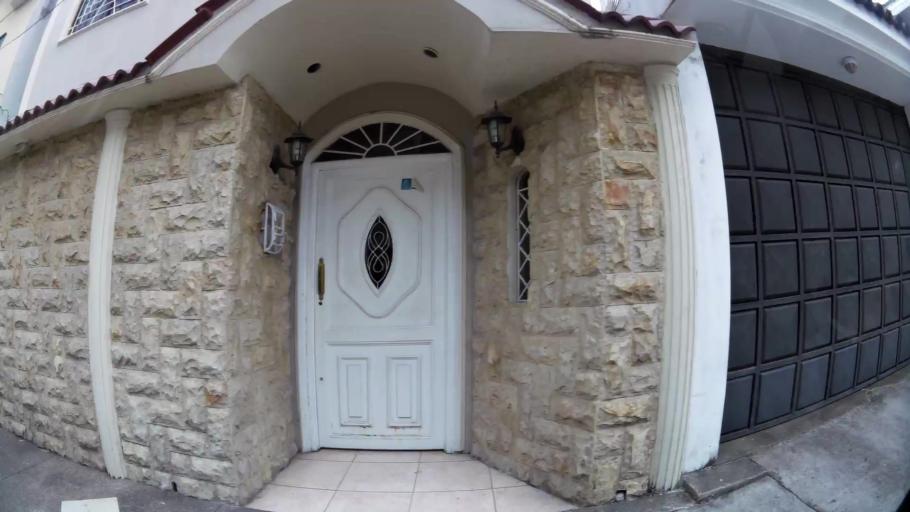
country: EC
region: Guayas
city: Eloy Alfaro
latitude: -2.1418
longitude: -79.8859
